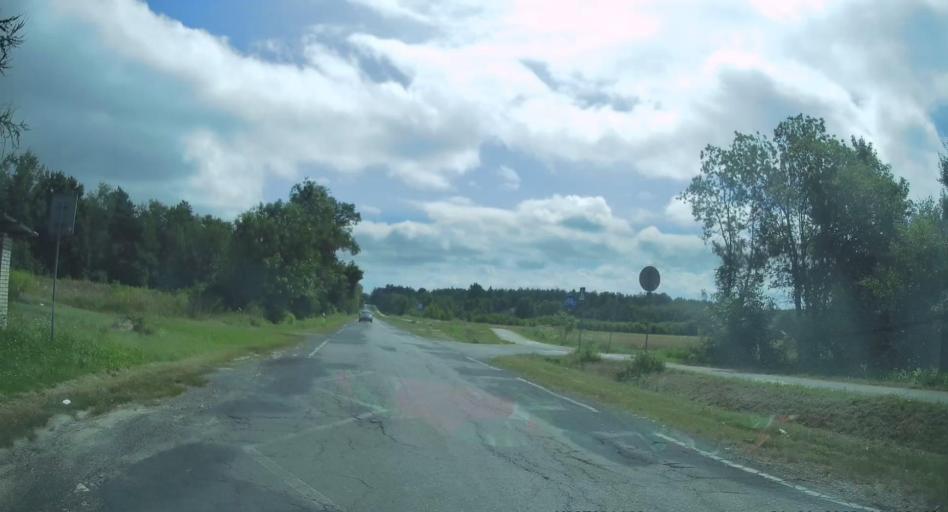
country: PL
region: Swietokrzyskie
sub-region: Powiat opatowski
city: Iwaniska
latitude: 50.7042
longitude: 21.3282
